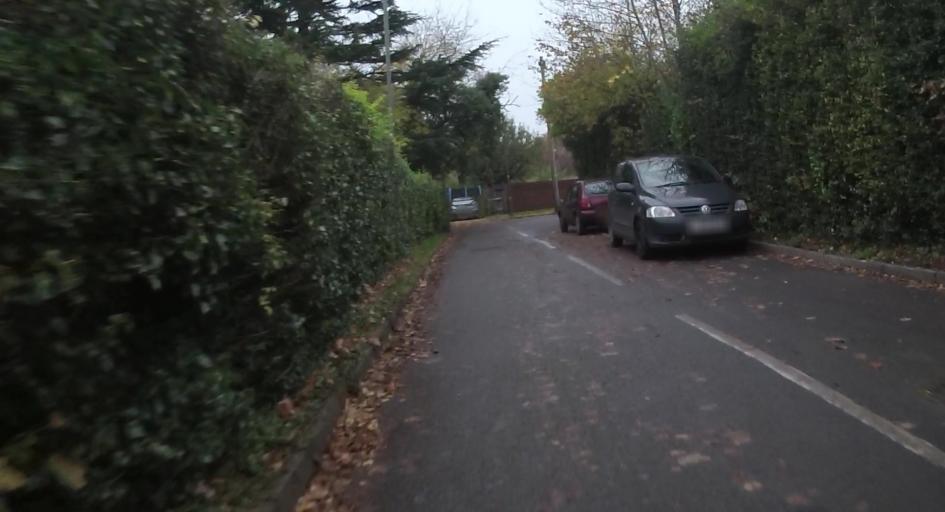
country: GB
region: England
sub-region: Surrey
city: Farnham
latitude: 51.1936
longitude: -0.8180
